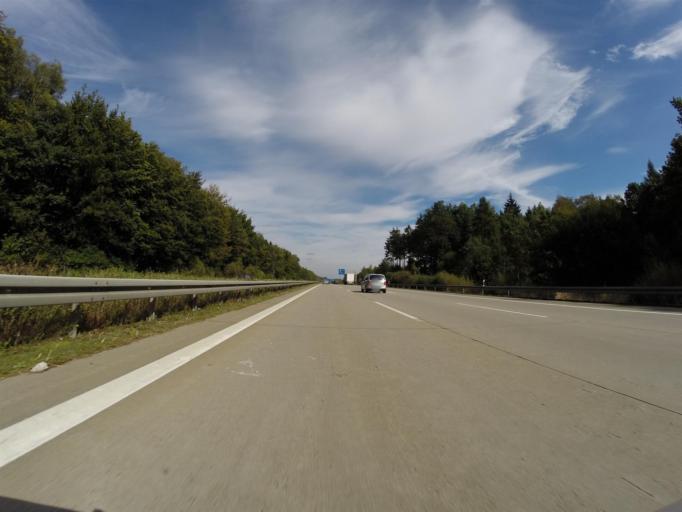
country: DE
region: Saxony
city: Rossau
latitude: 50.9732
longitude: 13.0862
